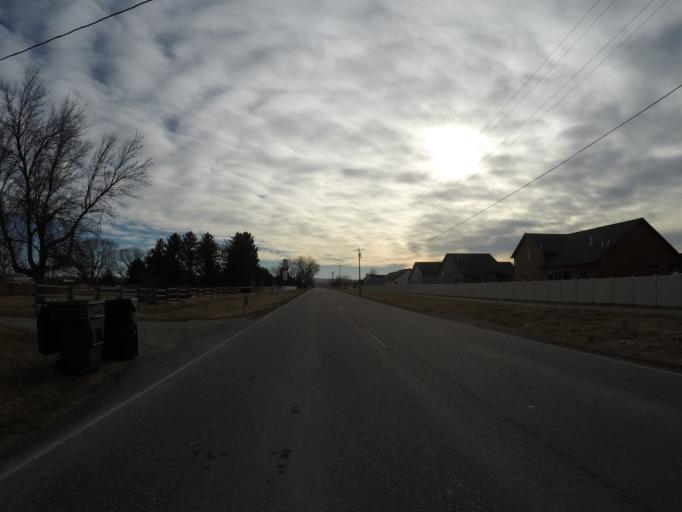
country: US
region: Montana
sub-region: Yellowstone County
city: Laurel
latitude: 45.7803
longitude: -108.6592
